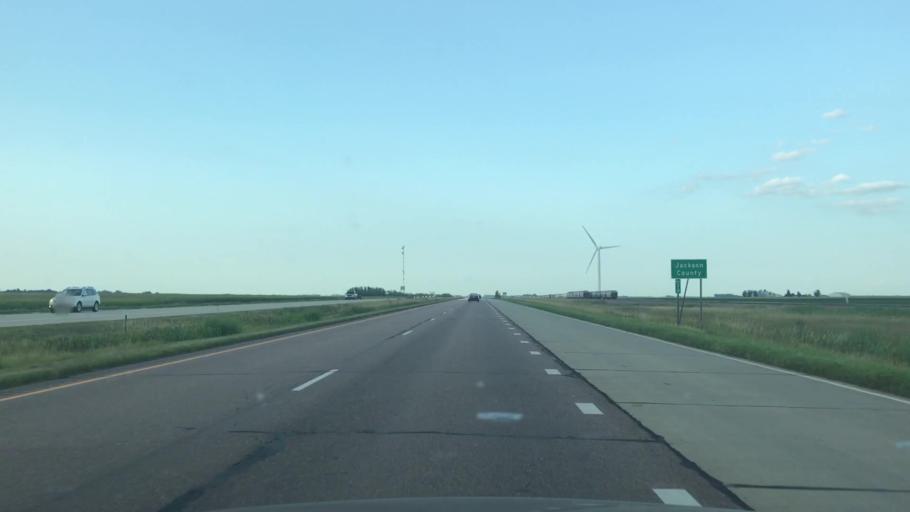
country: US
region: Minnesota
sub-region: Nobles County
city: Worthington
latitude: 43.7115
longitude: -95.4515
